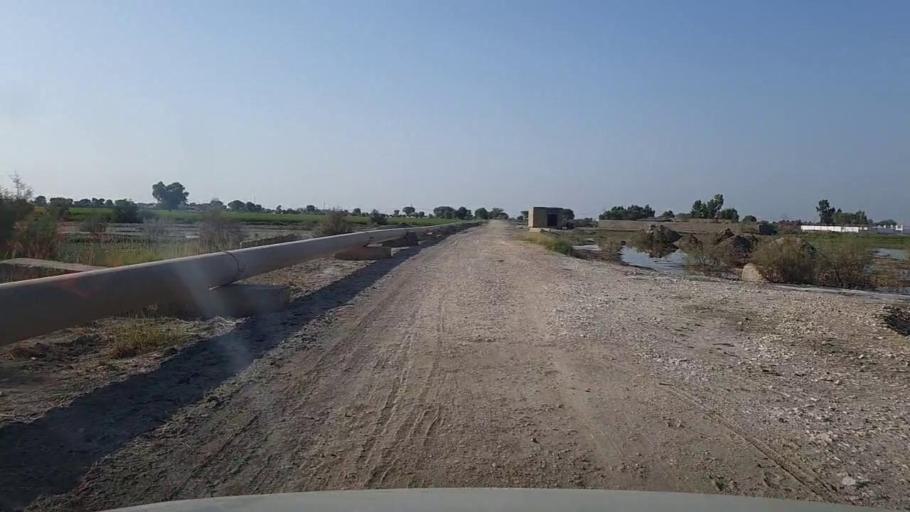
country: PK
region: Sindh
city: Kandhkot
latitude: 28.2849
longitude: 69.3341
